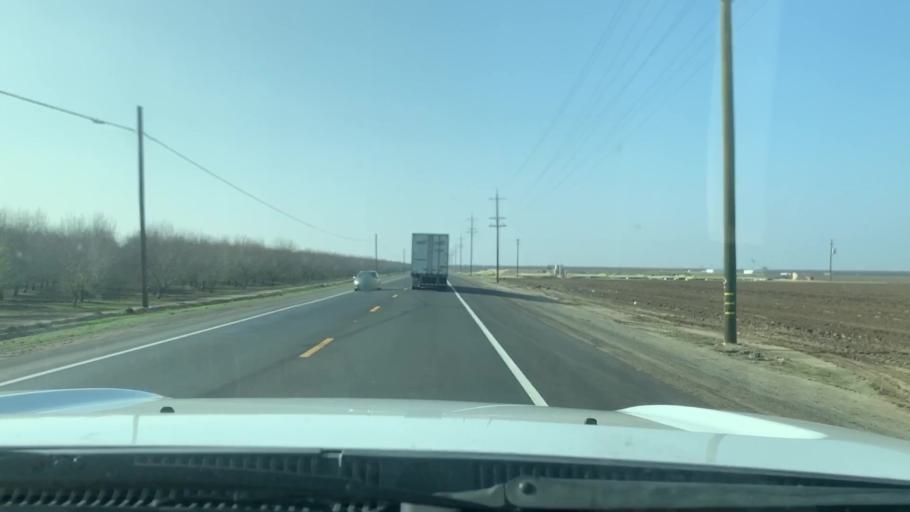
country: US
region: California
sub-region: Kern County
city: Wasco
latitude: 35.6017
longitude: -119.3014
